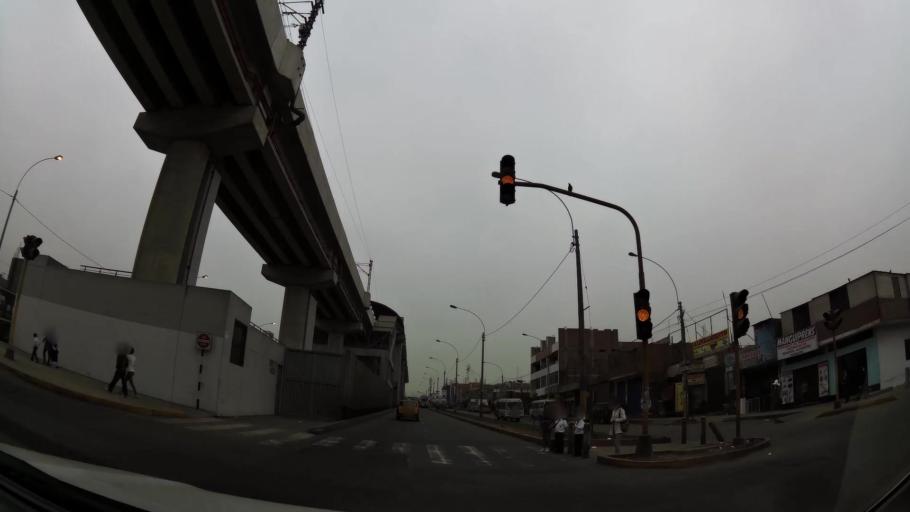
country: PE
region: Lima
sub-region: Lima
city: Independencia
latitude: -11.9609
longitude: -76.9882
